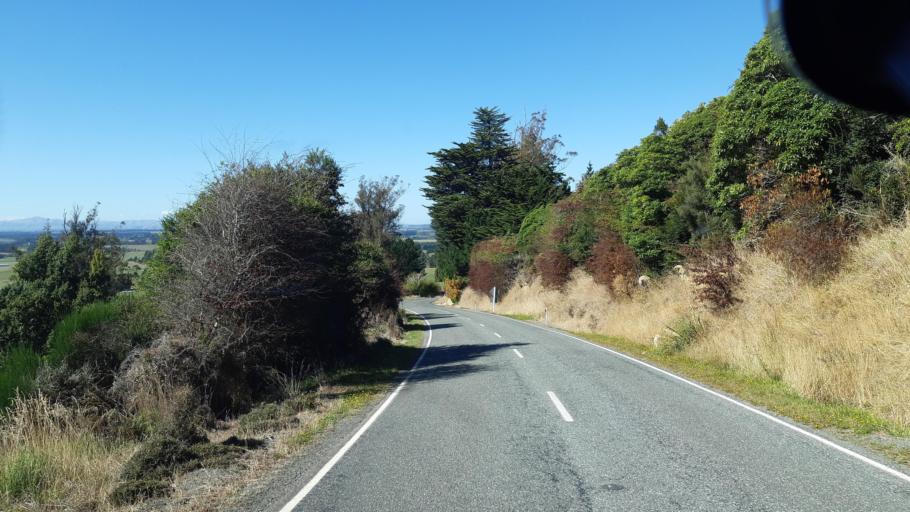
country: NZ
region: Southland
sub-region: Southland District
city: Winton
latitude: -45.8825
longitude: 168.4880
